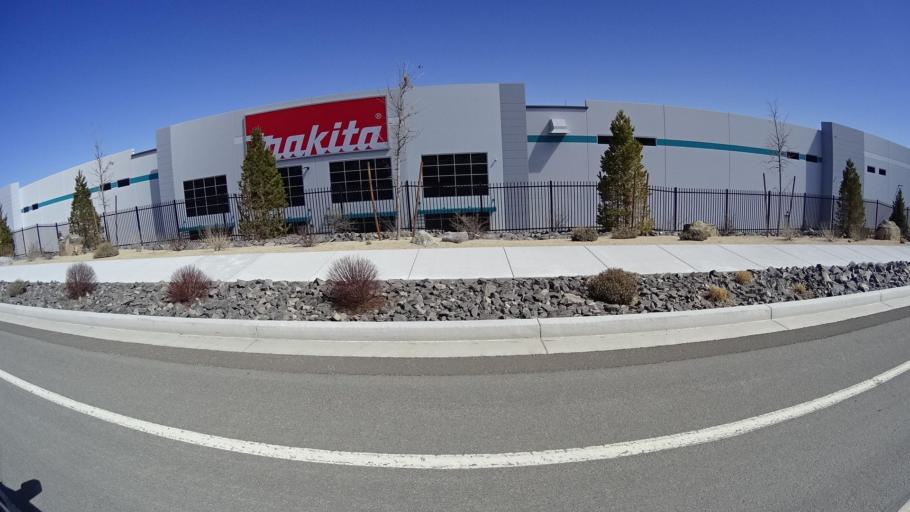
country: US
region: Nevada
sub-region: Washoe County
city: Lemmon Valley
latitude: 39.6506
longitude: -119.8700
